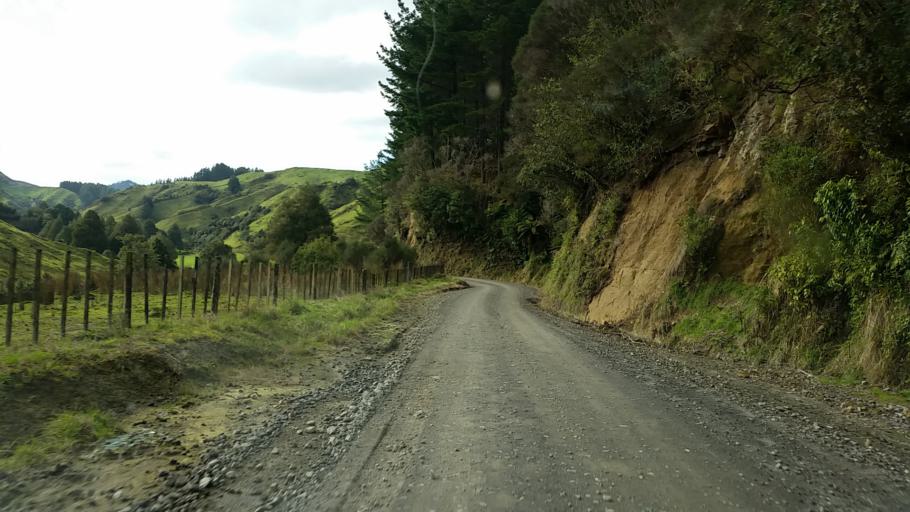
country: NZ
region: Taranaki
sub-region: New Plymouth District
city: Waitara
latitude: -39.1560
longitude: 174.5576
